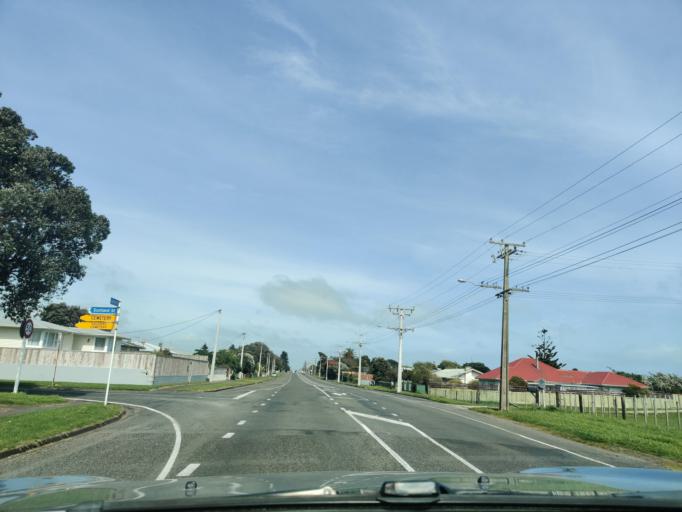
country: NZ
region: Taranaki
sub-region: South Taranaki District
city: Patea
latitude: -39.7466
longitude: 174.4653
